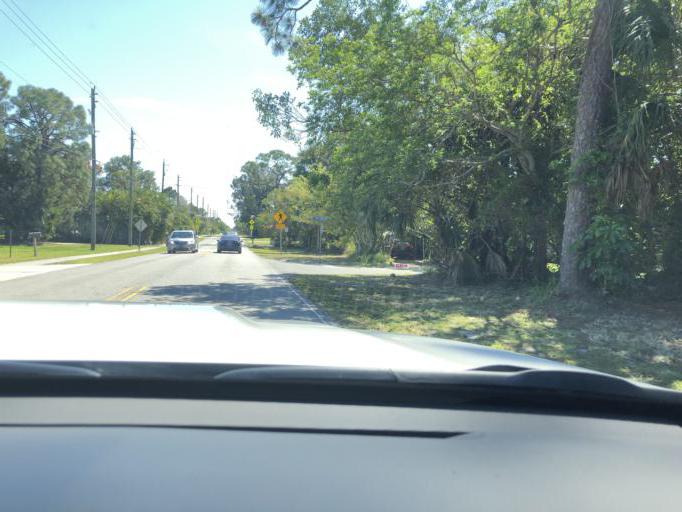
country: US
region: Florida
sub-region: Martin County
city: Stuart
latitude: 27.1860
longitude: -80.2571
